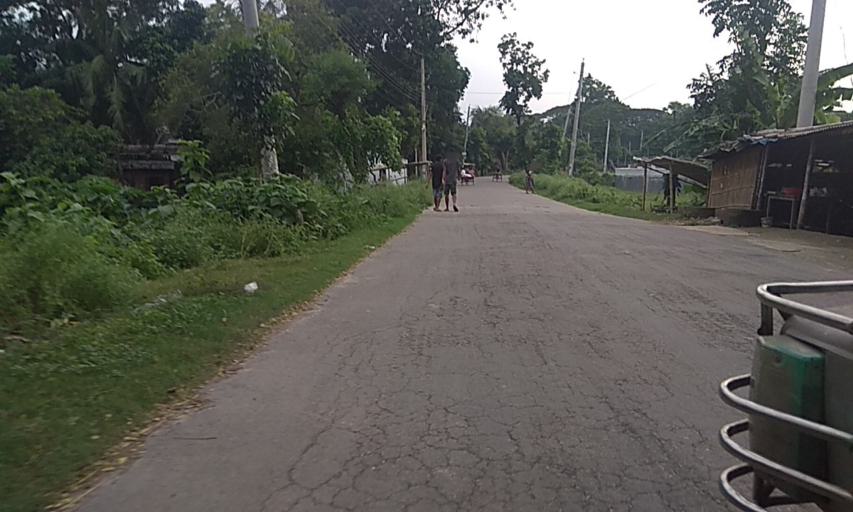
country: BD
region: Dhaka
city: Dohar
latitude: 23.4570
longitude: 90.0131
